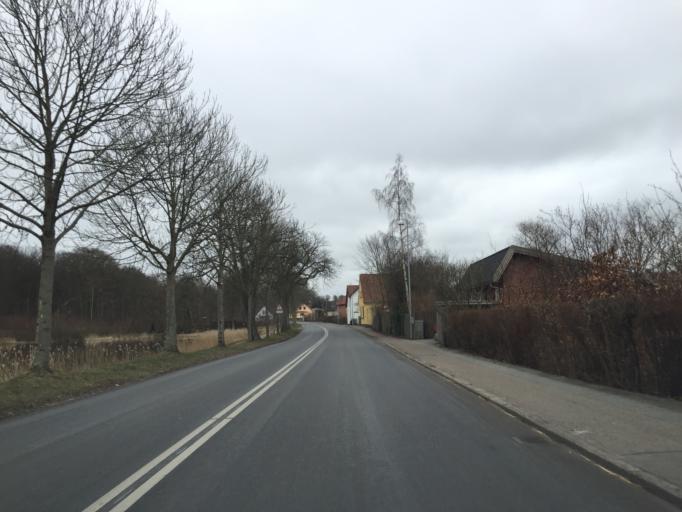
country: DK
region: Capital Region
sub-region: Hillerod Kommune
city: Hillerod
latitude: 55.9231
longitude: 12.3128
